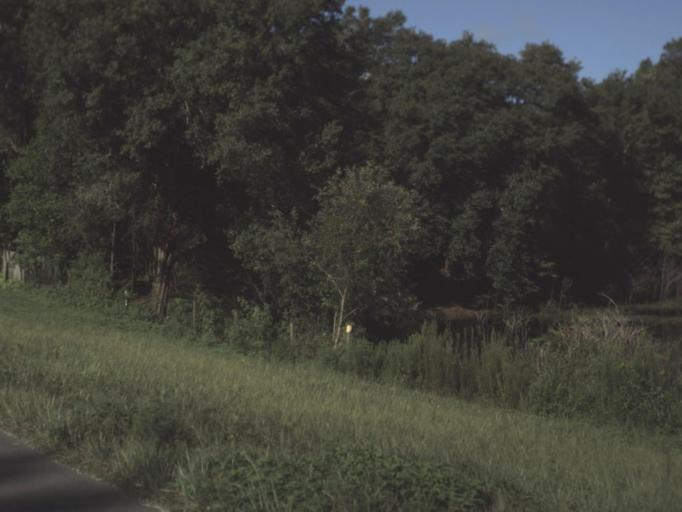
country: US
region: Florida
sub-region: Pasco County
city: Shady Hills
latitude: 28.3795
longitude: -82.4897
